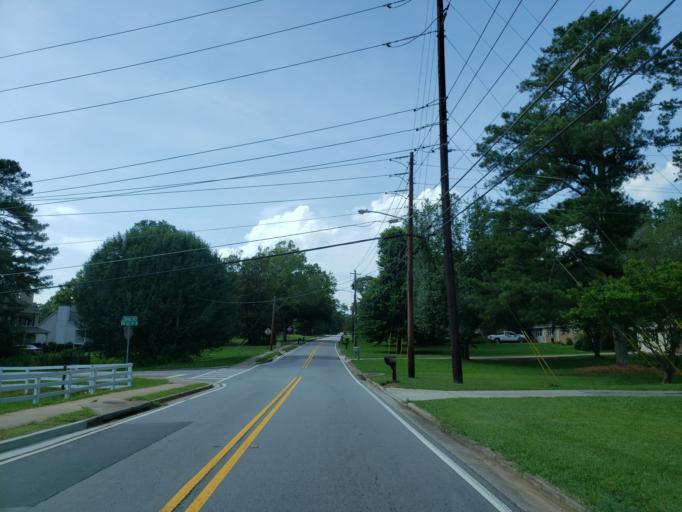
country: US
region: Georgia
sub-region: Cobb County
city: Powder Springs
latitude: 33.8804
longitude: -84.6838
